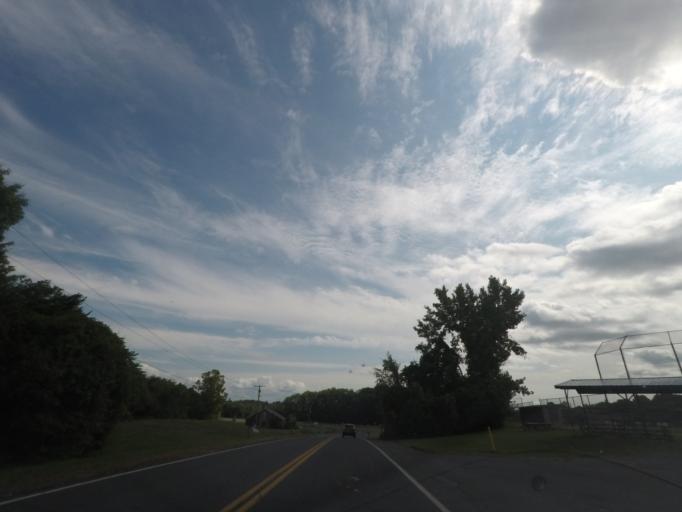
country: US
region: New York
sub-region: Albany County
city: Delmar
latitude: 42.6178
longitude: -73.7949
